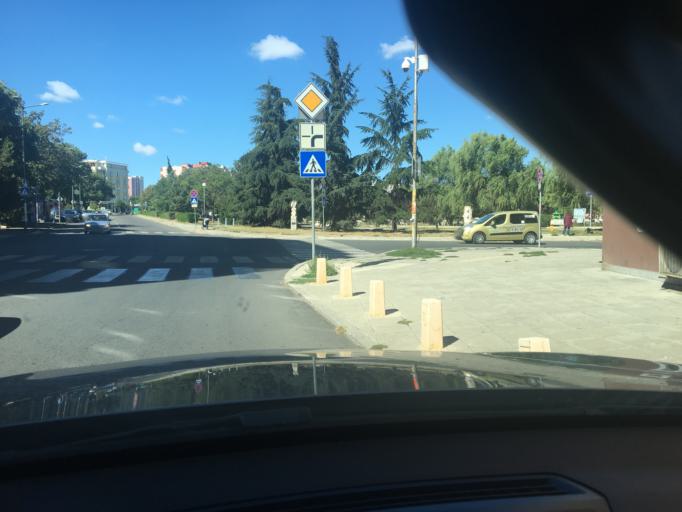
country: BG
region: Burgas
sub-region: Obshtina Burgas
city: Burgas
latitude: 42.5228
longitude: 27.4622
